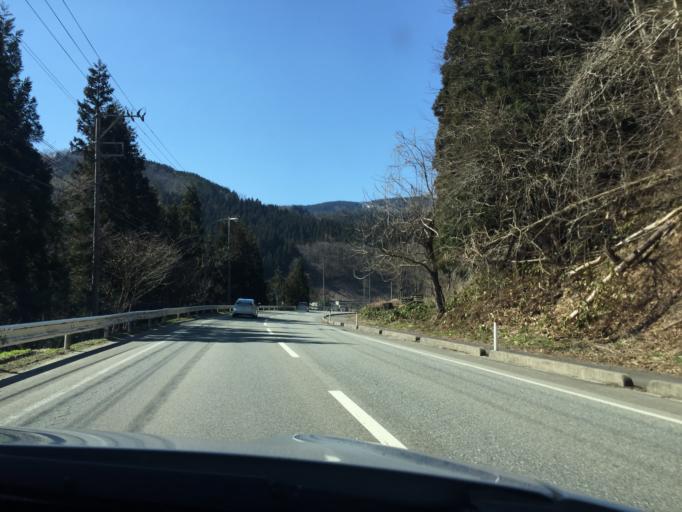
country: JP
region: Yamagata
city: Nagai
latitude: 38.2297
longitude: 140.0930
